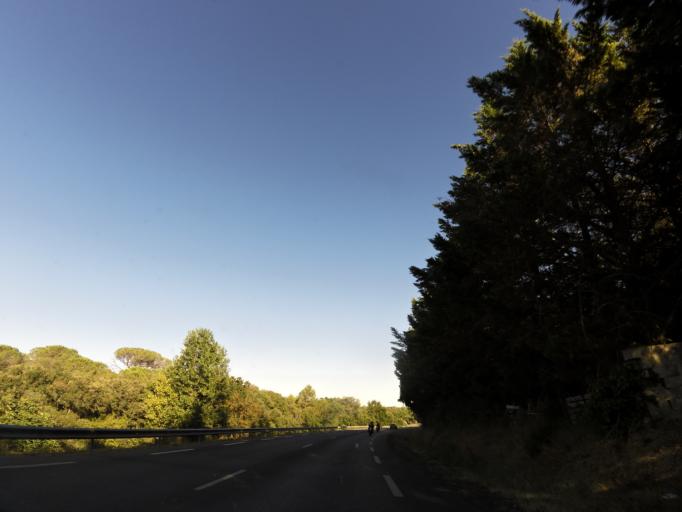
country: FR
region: Languedoc-Roussillon
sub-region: Departement du Gard
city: Villevieille
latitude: 43.7903
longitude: 4.1060
